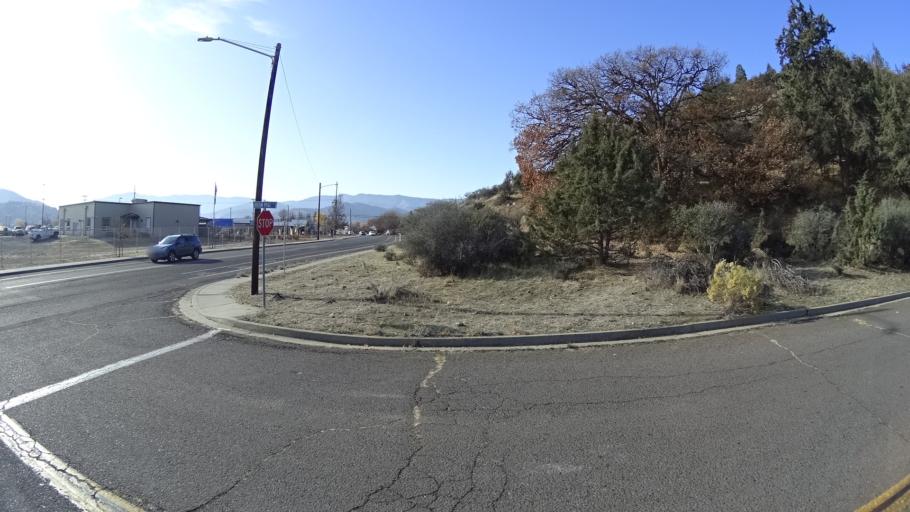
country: US
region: California
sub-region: Siskiyou County
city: Yreka
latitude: 41.7133
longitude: -122.6434
